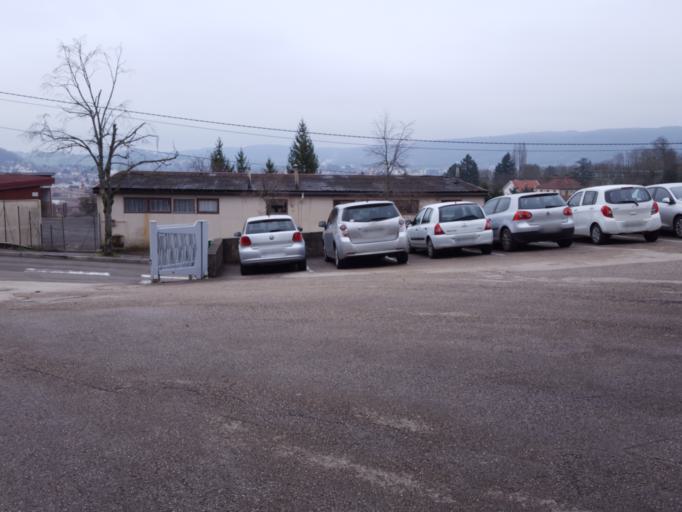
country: FR
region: Franche-Comte
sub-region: Departement du Jura
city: Lons-le-Saunier
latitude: 46.6647
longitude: 5.5415
